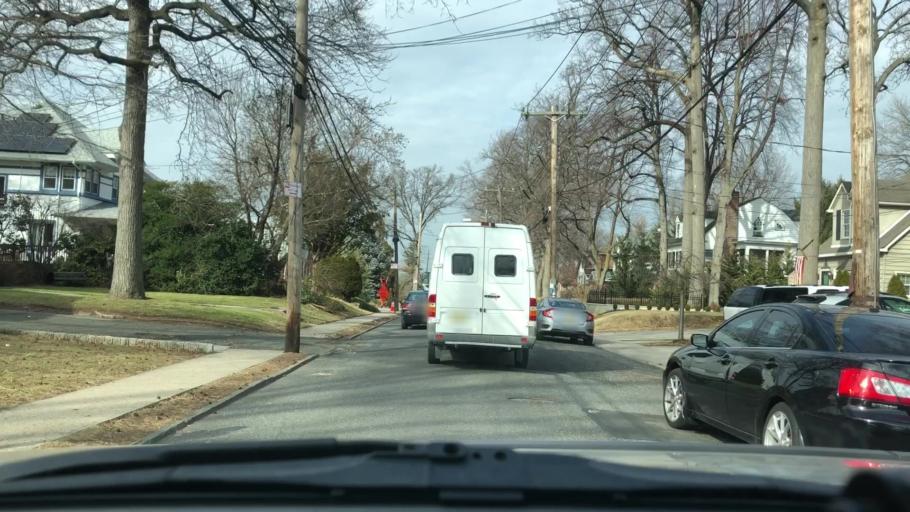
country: US
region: New Jersey
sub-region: Hudson County
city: Bayonne
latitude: 40.6323
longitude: -74.1061
